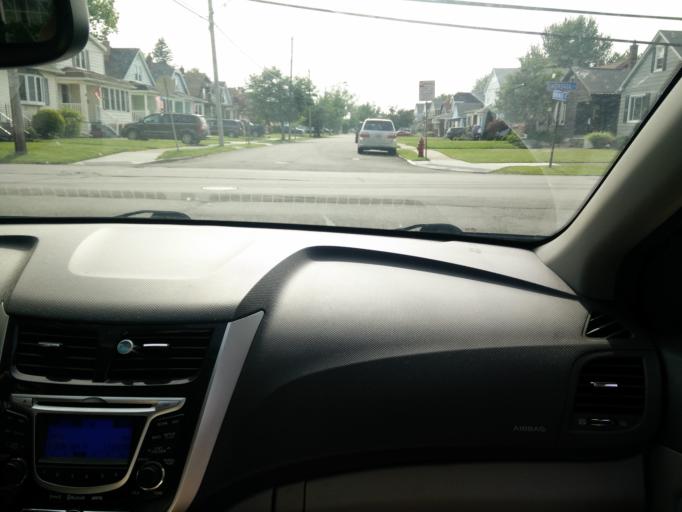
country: US
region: New York
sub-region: Erie County
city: West Seneca
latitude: 42.8365
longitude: -78.8008
